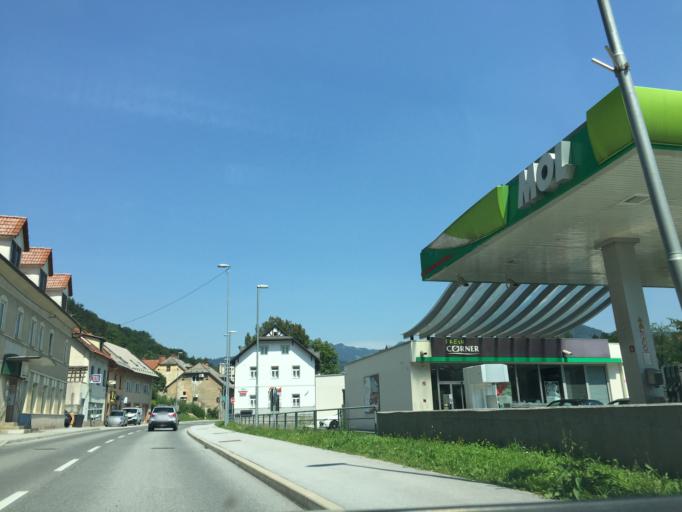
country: SI
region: Trbovlje
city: Trbovlje
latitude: 46.1427
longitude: 15.0358
